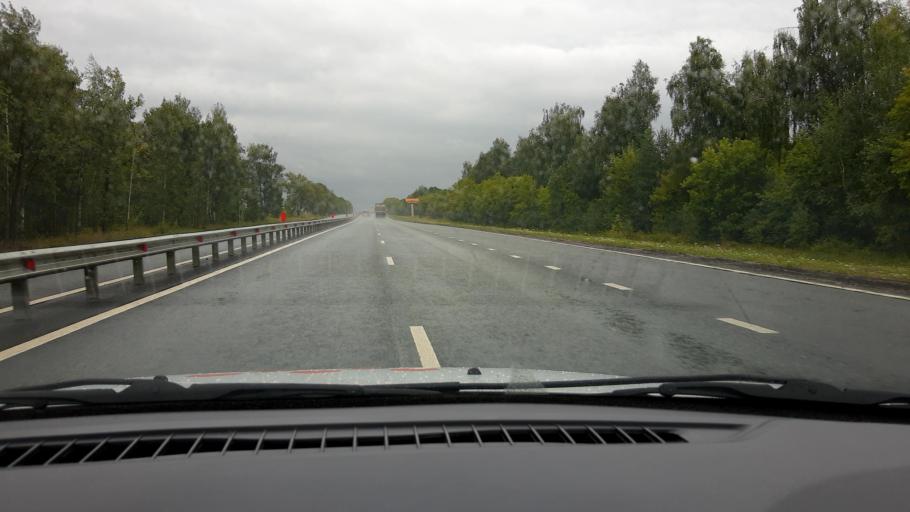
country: RU
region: Chuvashia
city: Yantikovo
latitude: 55.7921
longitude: 47.7903
